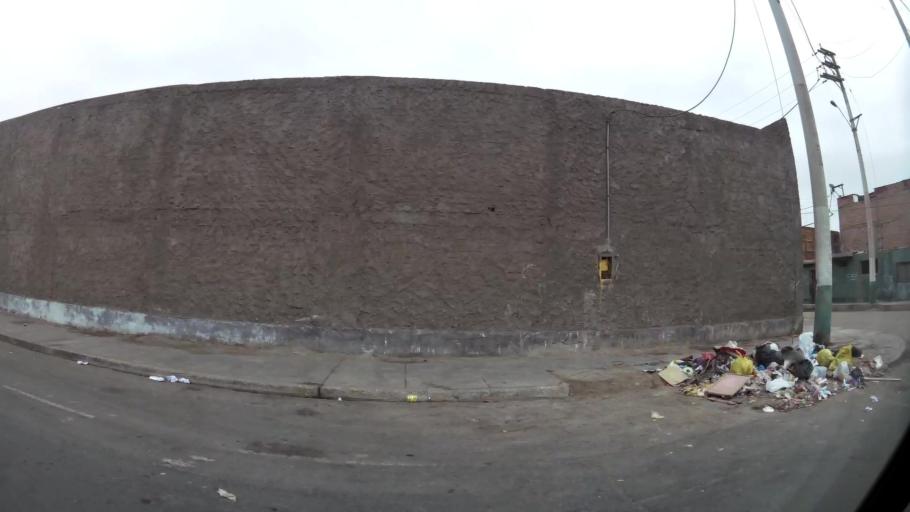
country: PE
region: Callao
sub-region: Callao
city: Callao
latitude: -12.0663
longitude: -77.1435
